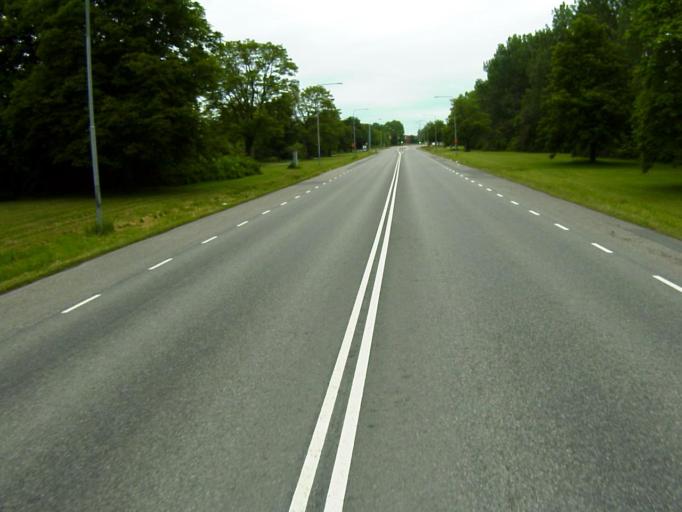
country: SE
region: Skane
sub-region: Kristianstads Kommun
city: Kristianstad
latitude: 56.0518
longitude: 14.1603
